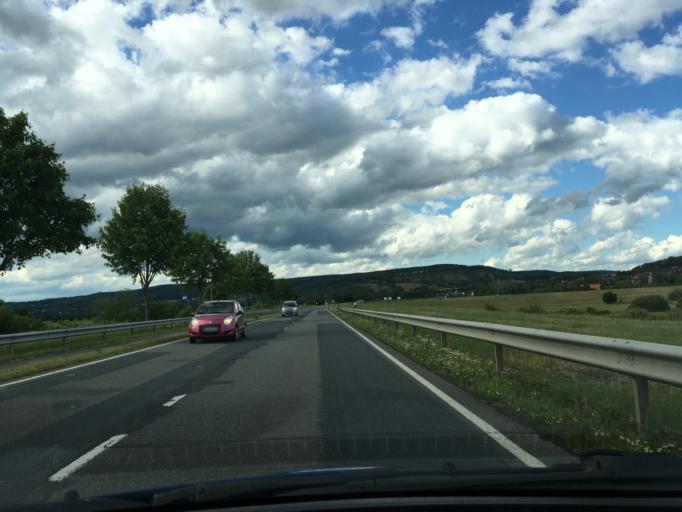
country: DE
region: Lower Saxony
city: Einbeck
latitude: 51.7922
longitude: 9.8983
